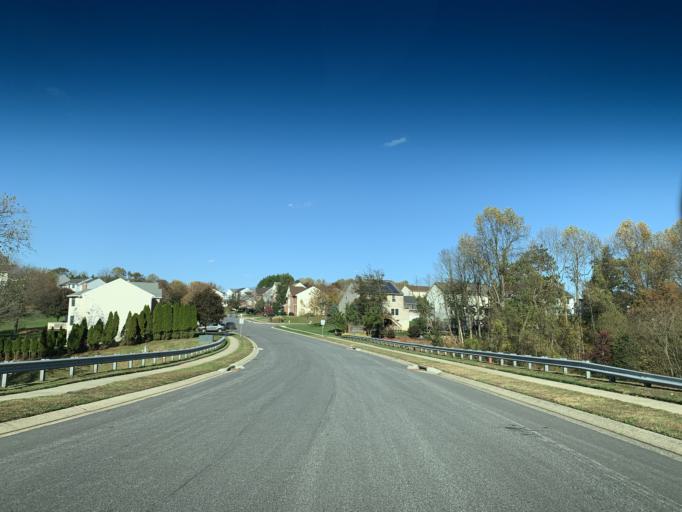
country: US
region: Maryland
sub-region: Harford County
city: Bel Air South
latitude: 39.5022
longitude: -76.3144
